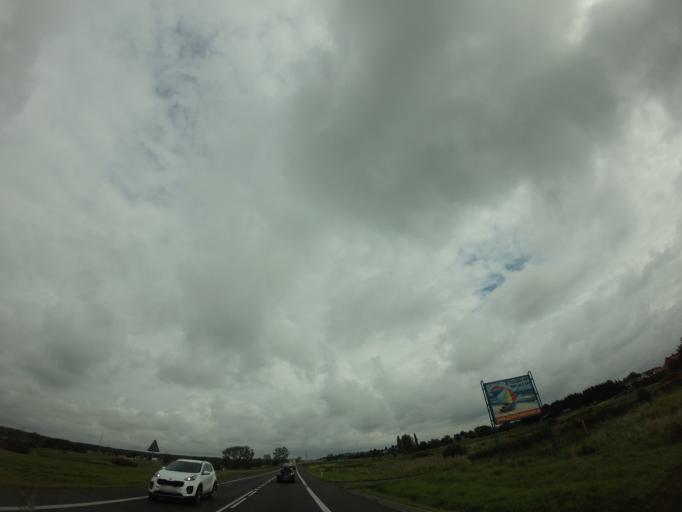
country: PL
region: West Pomeranian Voivodeship
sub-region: Powiat goleniowski
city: Przybiernow
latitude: 53.7520
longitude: 14.7743
